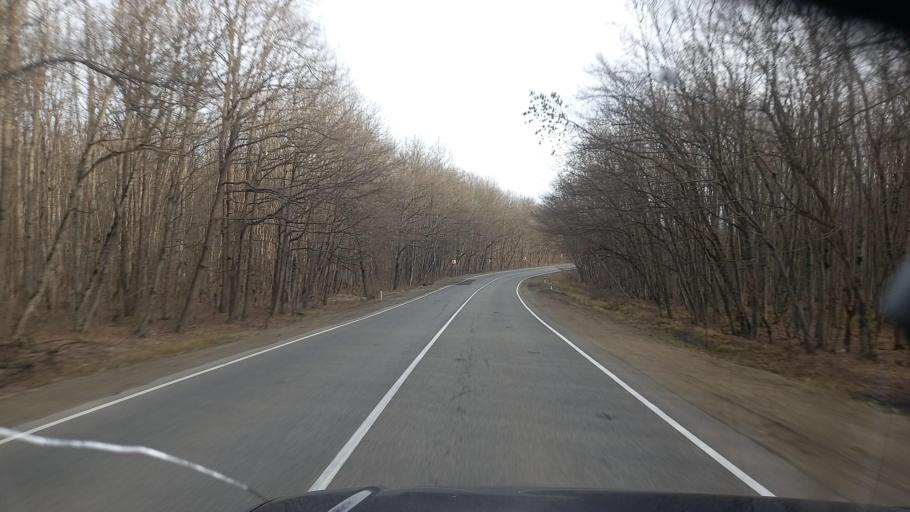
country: RU
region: Krasnodarskiy
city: Khadyzhensk
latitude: 44.6552
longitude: 39.4816
